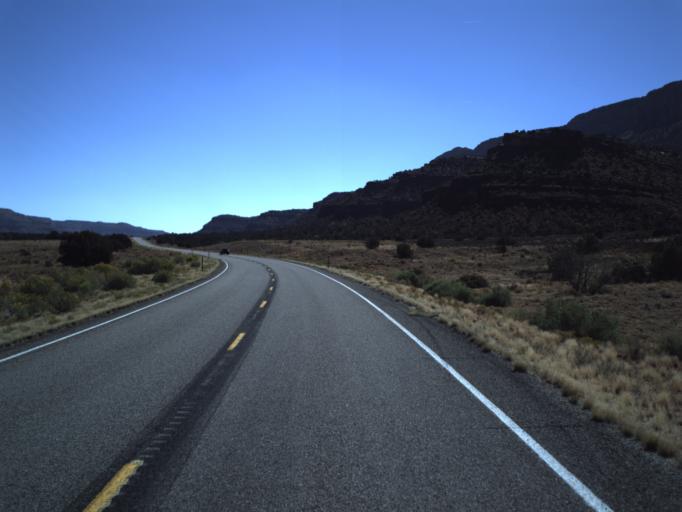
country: US
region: Utah
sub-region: San Juan County
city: Blanding
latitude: 37.6800
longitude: -110.2176
